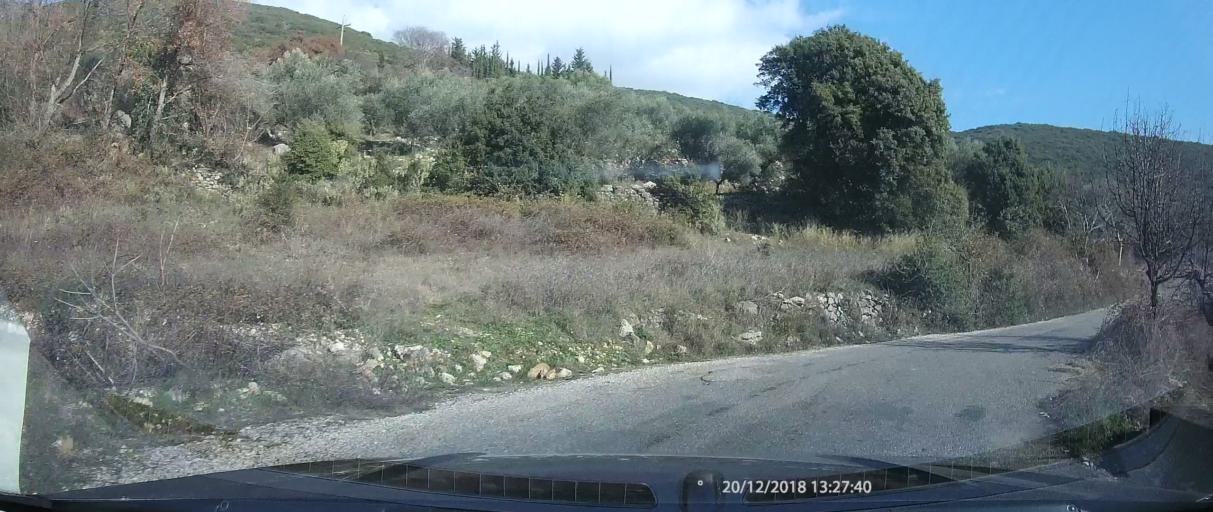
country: GR
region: West Greece
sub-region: Nomos Aitolias kai Akarnanias
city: Paravola
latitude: 38.6307
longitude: 21.5701
